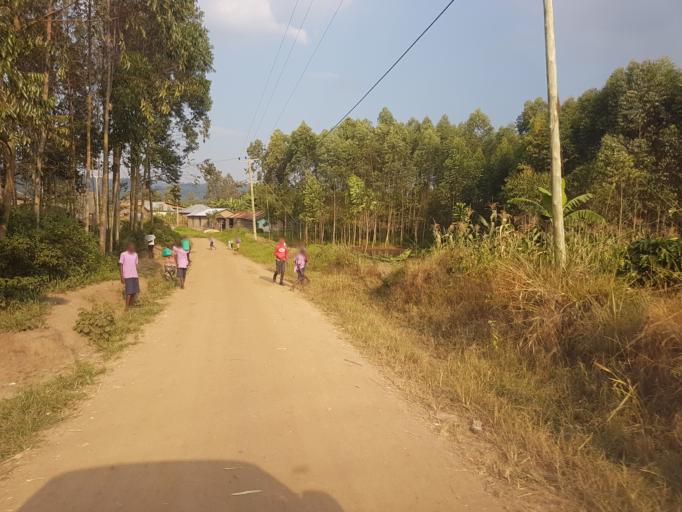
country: UG
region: Western Region
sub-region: Rukungiri District
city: Rukungiri
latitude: -0.6707
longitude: 29.8820
